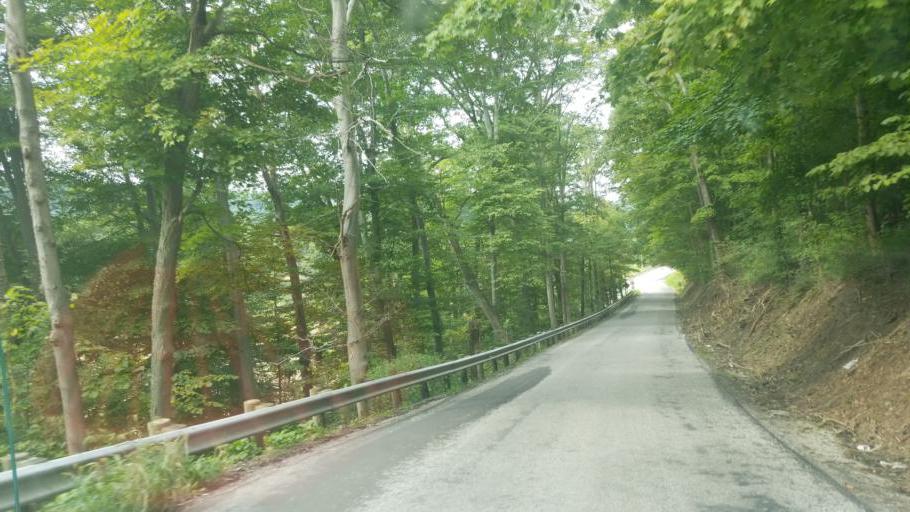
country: US
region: Ohio
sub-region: Wayne County
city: Wooster
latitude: 40.9012
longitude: -82.0072
